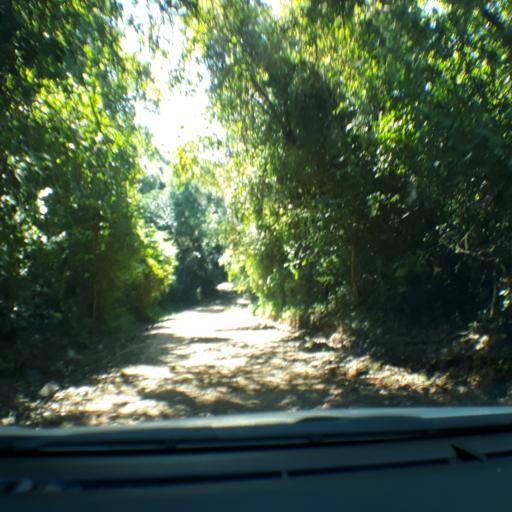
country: AR
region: Misiones
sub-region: Departamento de San Ignacio
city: San Ignacio
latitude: -27.2827
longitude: -55.5675
